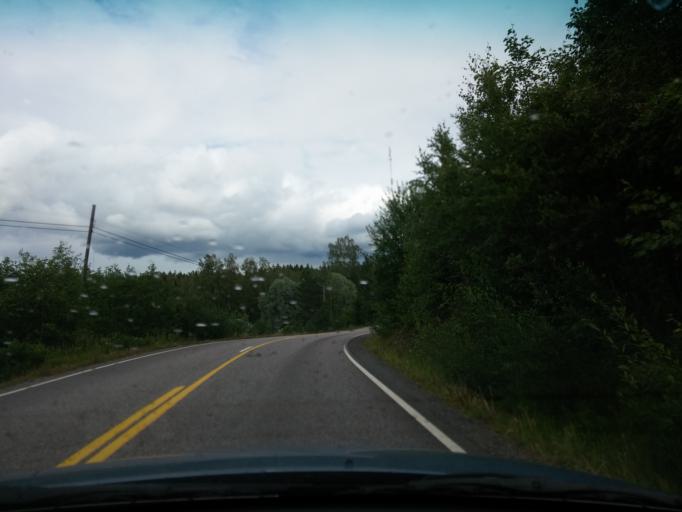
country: FI
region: Uusimaa
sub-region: Porvoo
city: Askola
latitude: 60.5506
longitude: 25.6710
